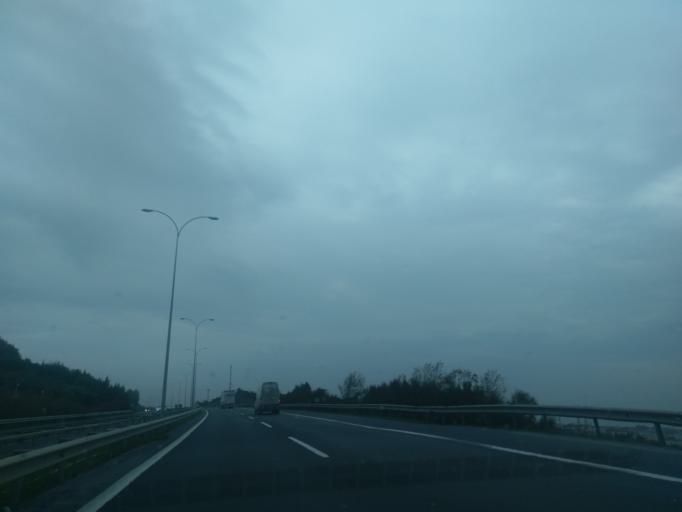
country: TR
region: Istanbul
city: Celaliye
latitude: 41.0594
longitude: 28.4122
